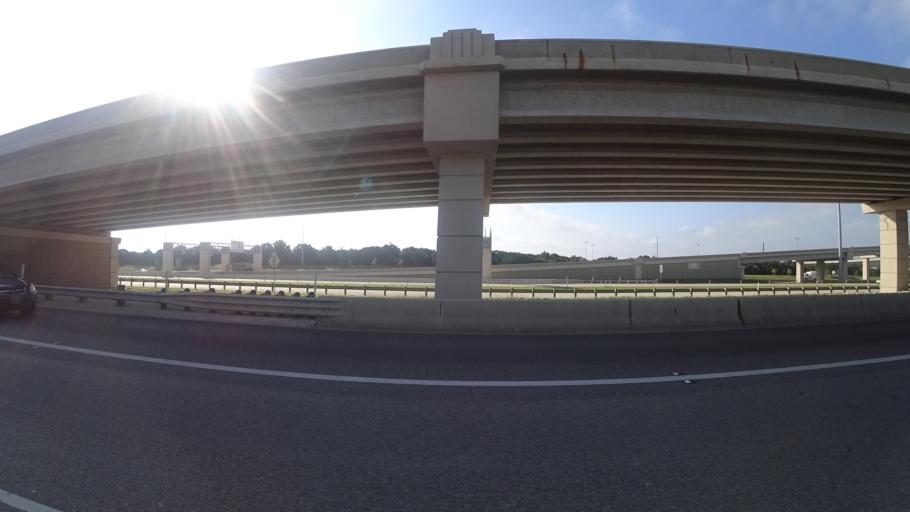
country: US
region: Texas
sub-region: Travis County
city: Austin
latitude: 30.3277
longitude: -97.6678
